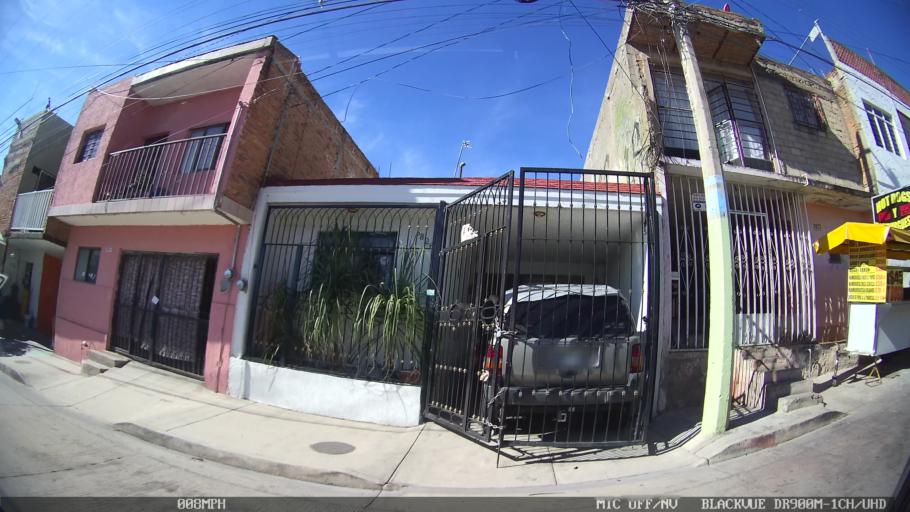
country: MX
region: Jalisco
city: Tlaquepaque
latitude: 20.6933
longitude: -103.2765
